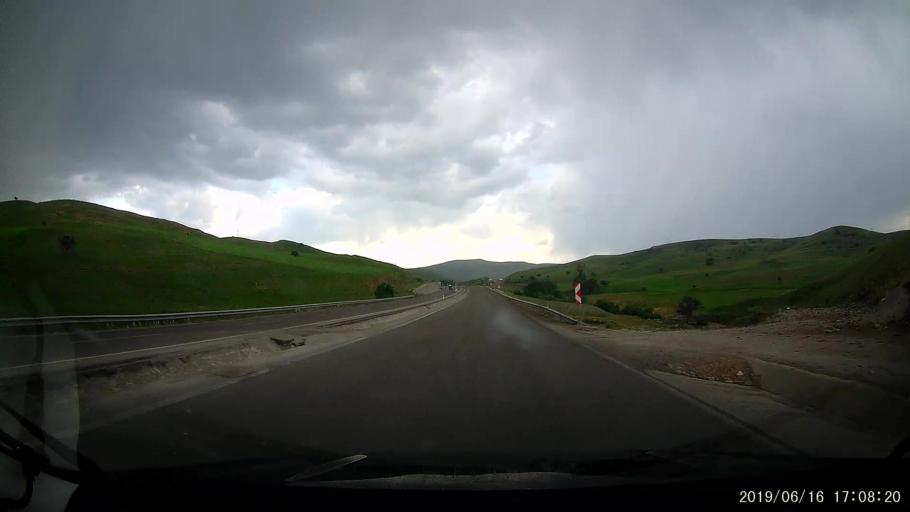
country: TR
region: Erzurum
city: Askale
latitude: 39.9106
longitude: 40.6624
